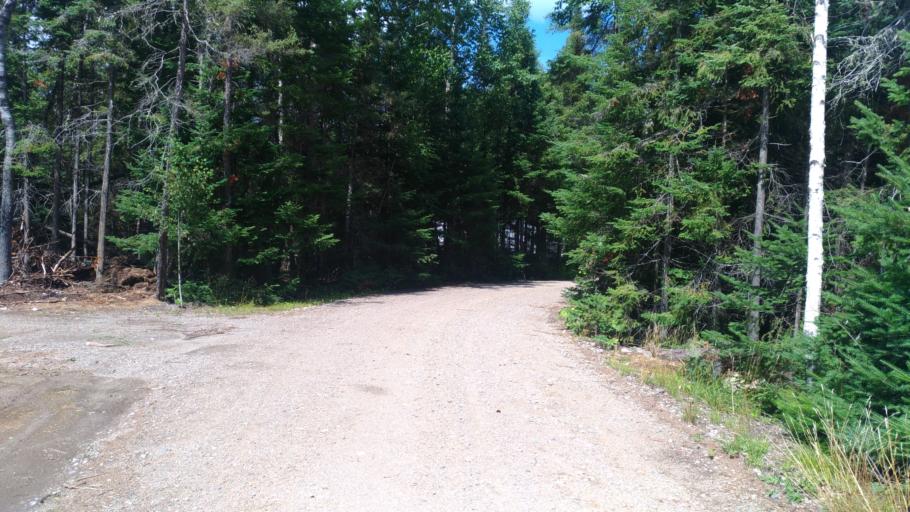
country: CA
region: Ontario
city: Rayside-Balfour
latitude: 46.5849
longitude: -81.5454
